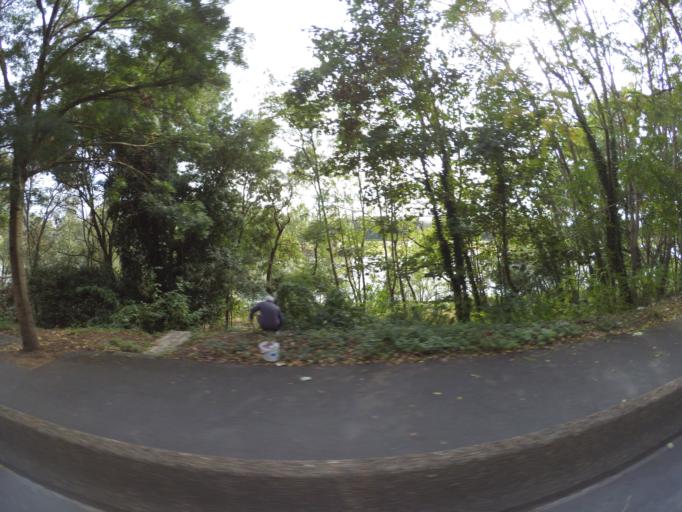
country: FR
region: Centre
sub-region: Departement d'Indre-et-Loire
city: Saint-Cyr-sur-Loire
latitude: 47.3969
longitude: 0.6630
